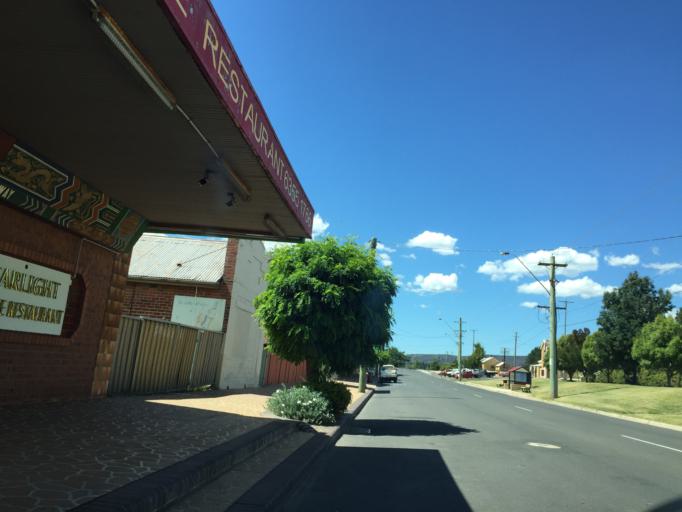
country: AU
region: New South Wales
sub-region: Lithgow
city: Portland
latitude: -33.4083
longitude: 150.0669
